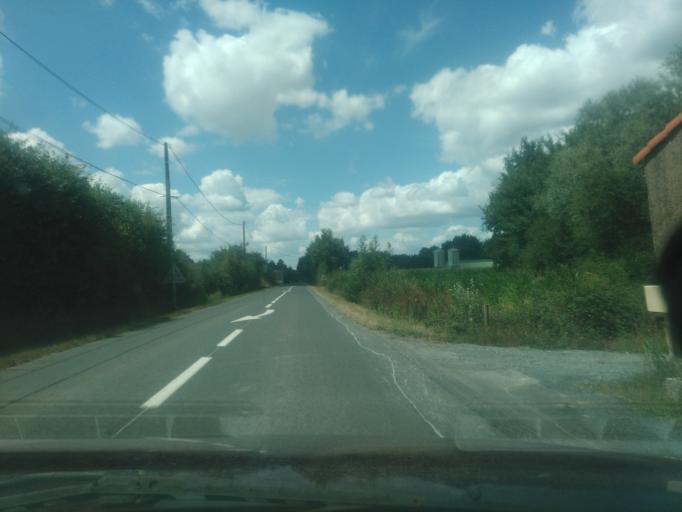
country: FR
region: Pays de la Loire
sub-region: Departement de la Vendee
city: Chauche
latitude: 46.8385
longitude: -1.2849
